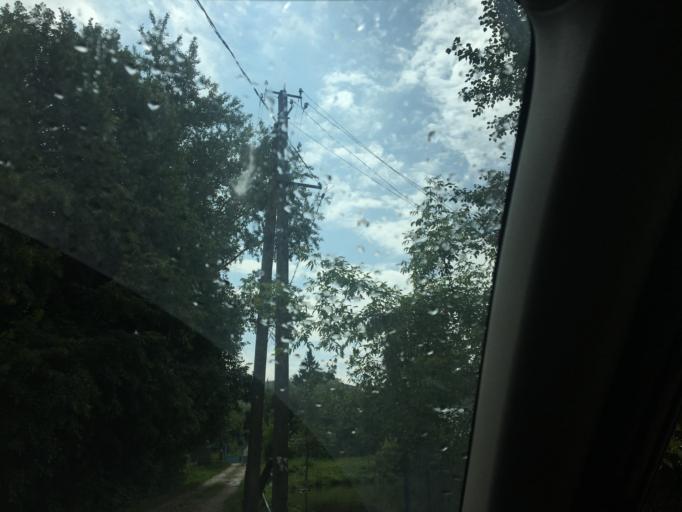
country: RU
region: Tula
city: Mendeleyevskiy
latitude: 54.1489
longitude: 37.5870
